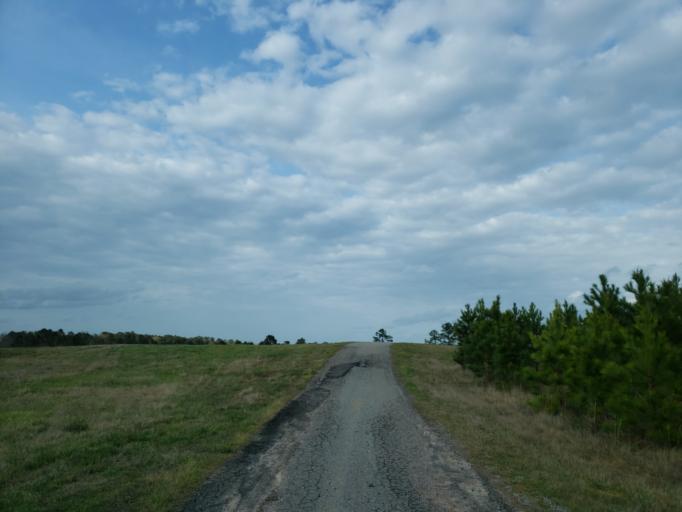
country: US
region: Mississippi
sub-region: Jones County
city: Ellisville
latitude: 31.5621
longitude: -89.2514
